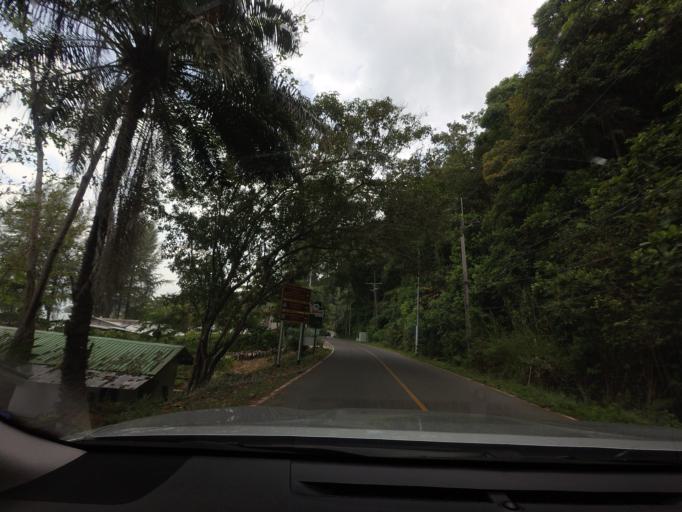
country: TH
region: Phangnga
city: Ban Ao Nang
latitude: 8.0881
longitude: 98.7465
